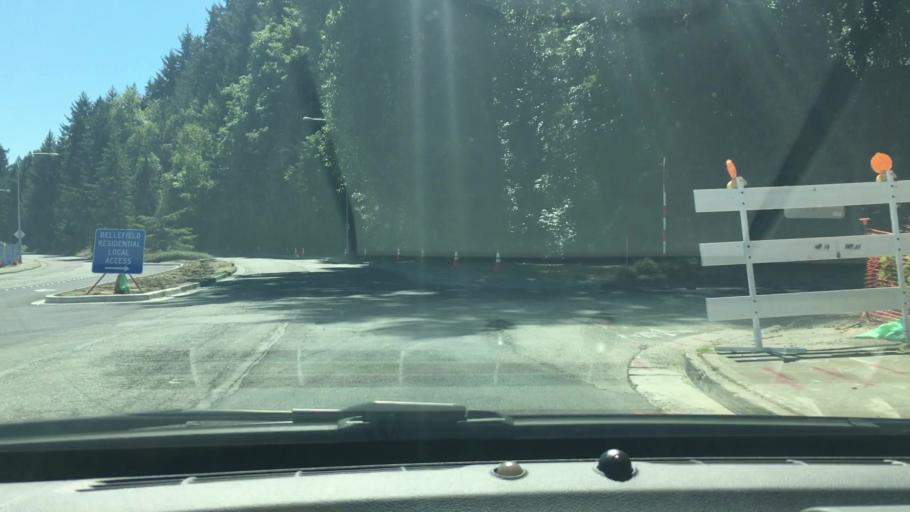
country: US
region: Washington
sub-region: King County
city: Bellevue
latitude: 47.5976
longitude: -122.1933
